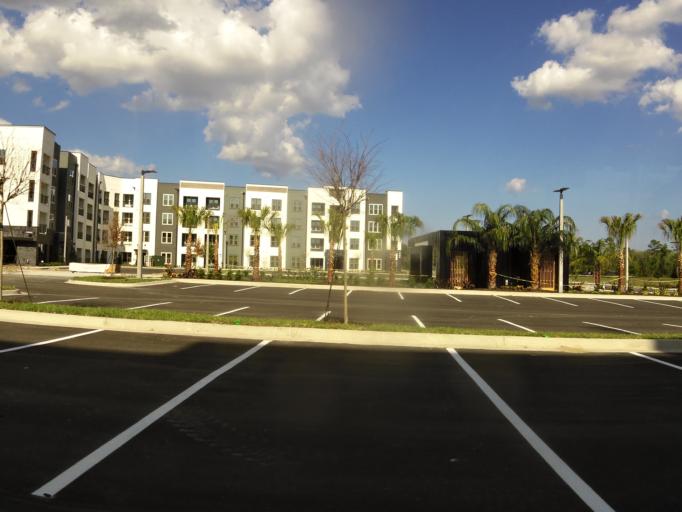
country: US
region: Florida
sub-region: Saint Johns County
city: Palm Valley
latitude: 30.1645
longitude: -81.5079
